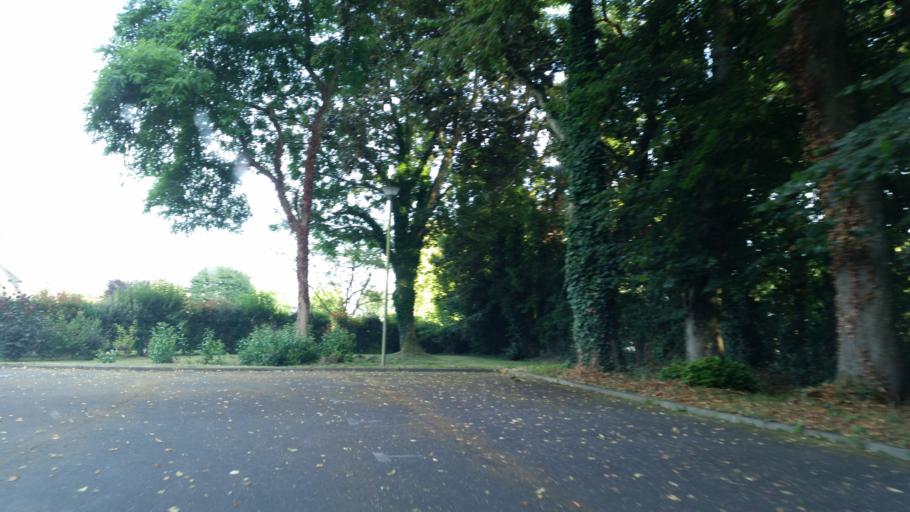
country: FR
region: Lower Normandy
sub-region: Departement du Calvados
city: La Riviere-Saint-Sauveur
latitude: 49.3787
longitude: 0.2484
